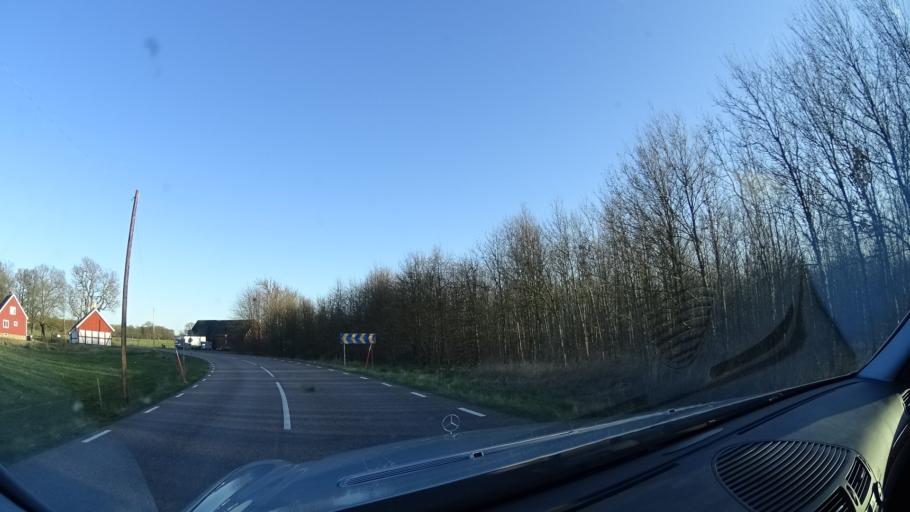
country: SE
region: Skane
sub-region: Svalovs Kommun
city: Kagerod
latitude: 55.9811
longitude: 13.1224
